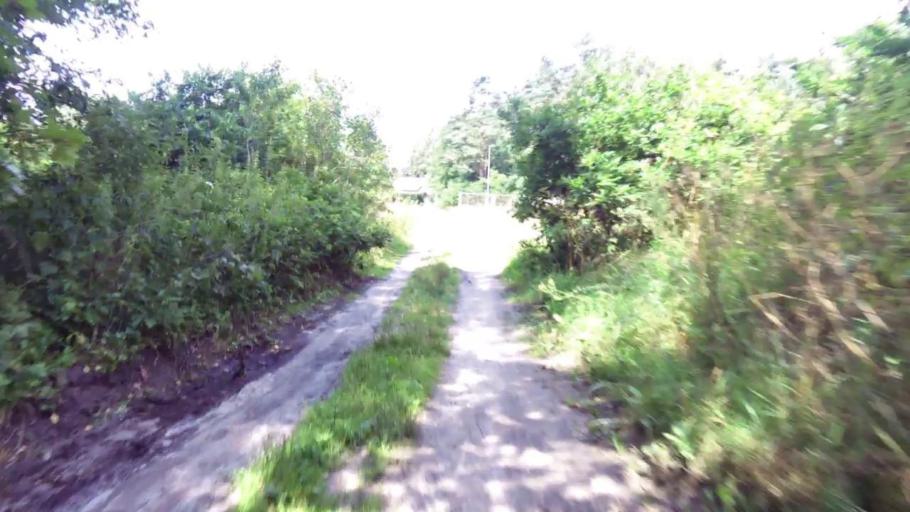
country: PL
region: West Pomeranian Voivodeship
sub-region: Powiat gryfinski
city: Stare Czarnowo
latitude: 53.3558
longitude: 14.7518
